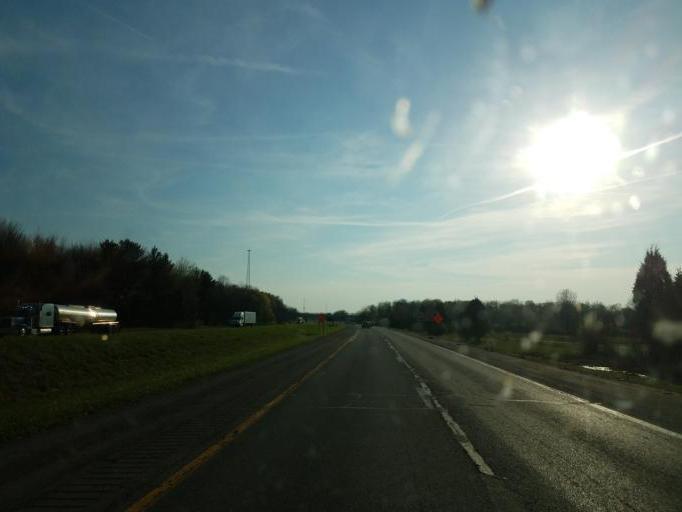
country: US
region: Ohio
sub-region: Warren County
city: Waynesville
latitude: 39.4371
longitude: -84.0650
